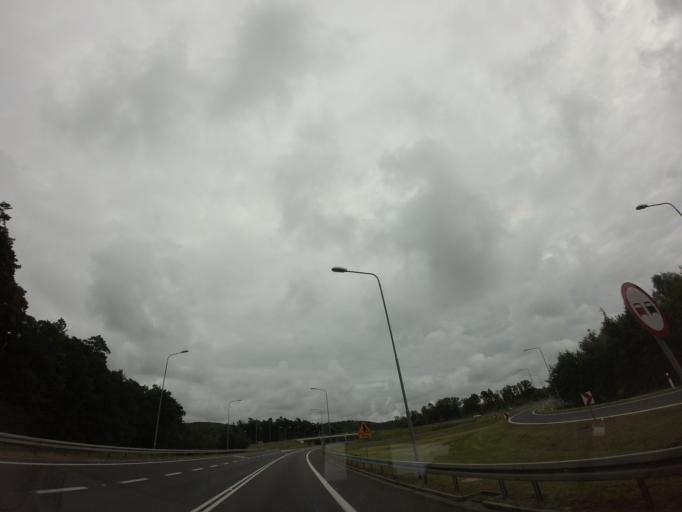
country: PL
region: West Pomeranian Voivodeship
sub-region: Powiat kamienski
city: Miedzyzdroje
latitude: 53.9137
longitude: 14.4256
